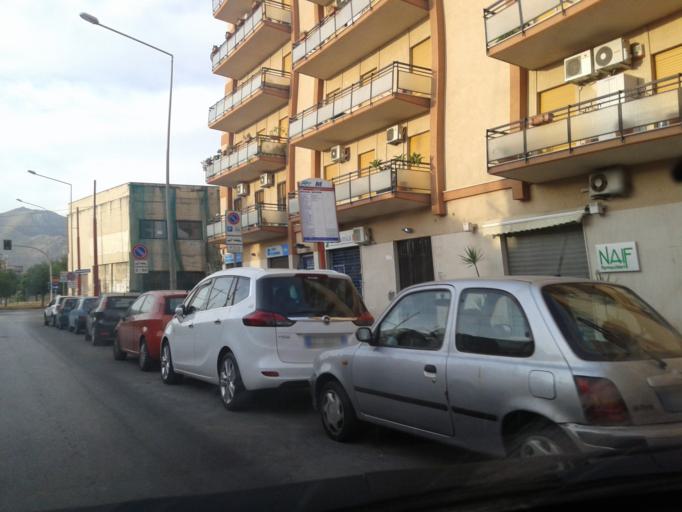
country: IT
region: Sicily
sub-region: Palermo
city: Palermo
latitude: 38.1037
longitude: 13.3297
